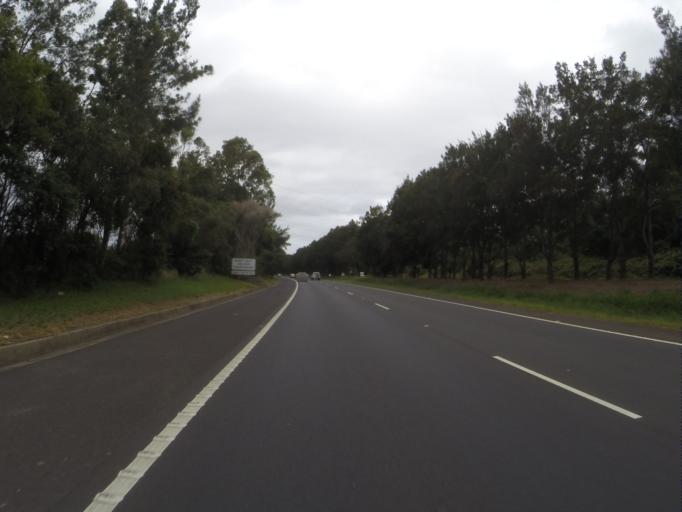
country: AU
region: New South Wales
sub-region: Wollongong
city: Berkeley
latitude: -34.4646
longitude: 150.8482
